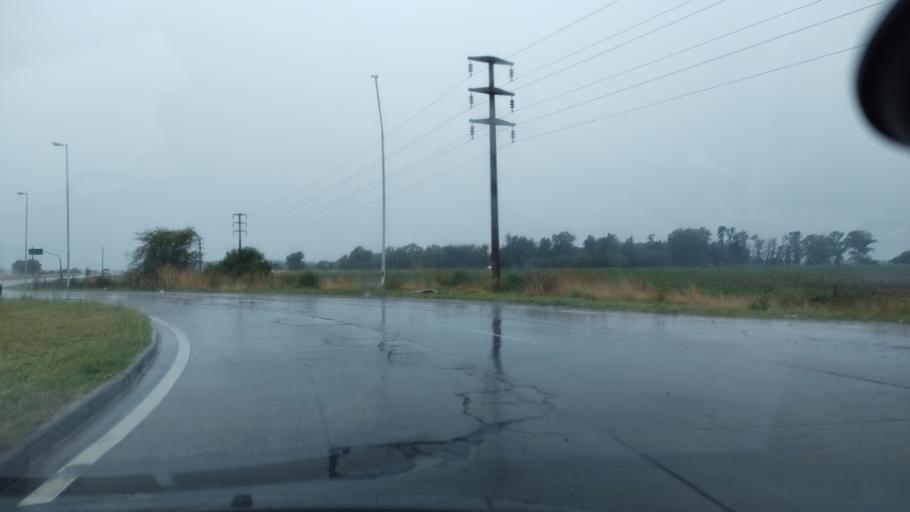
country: AR
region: Buenos Aires
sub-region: Partido de San Vicente
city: San Vicente
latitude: -35.0687
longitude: -58.5078
